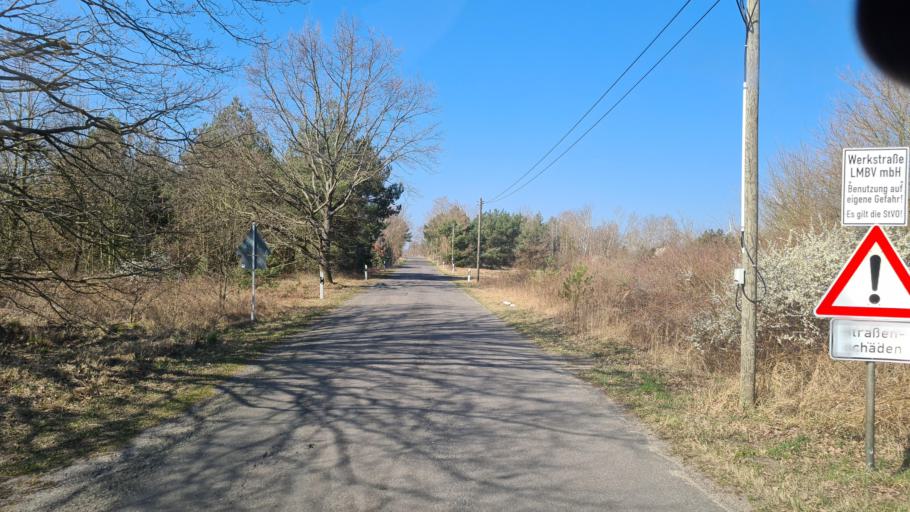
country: DE
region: Brandenburg
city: Vetschau
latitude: 51.7879
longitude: 14.0219
